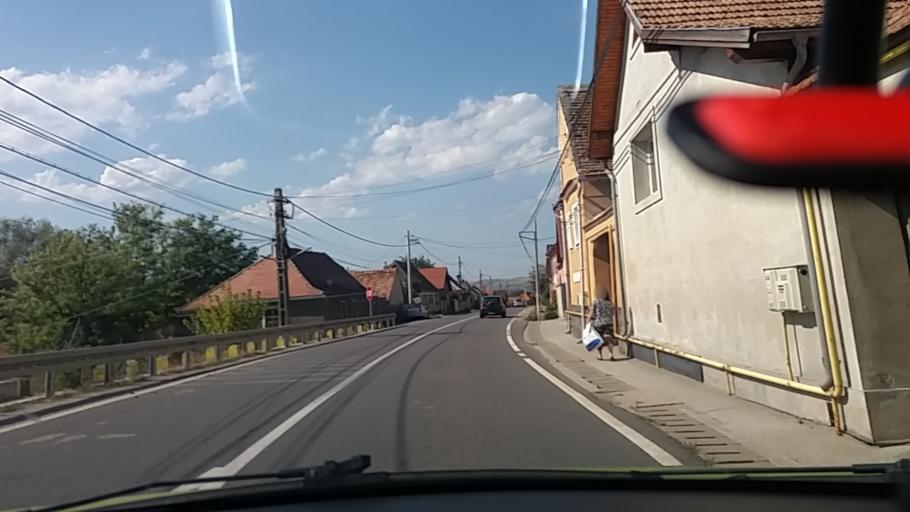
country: RO
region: Sibiu
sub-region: Comuna Slimnic
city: Slimnic
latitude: 45.9589
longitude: 24.1657
